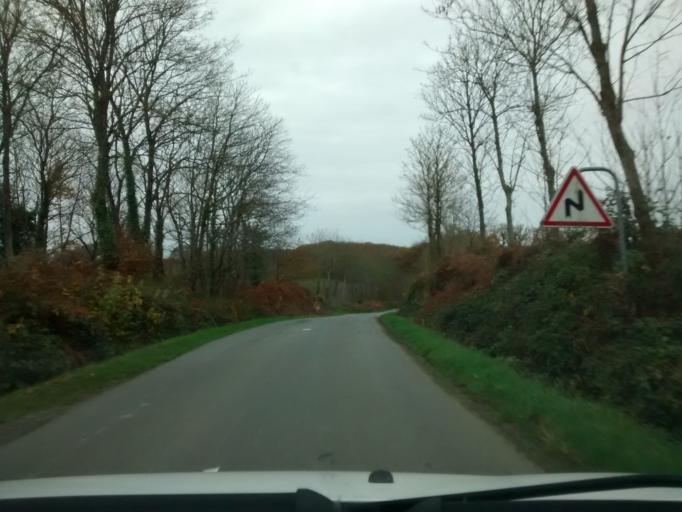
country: FR
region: Brittany
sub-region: Departement d'Ille-et-Vilaine
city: Argentre-du-Plessis
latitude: 48.0762
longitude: -1.1625
